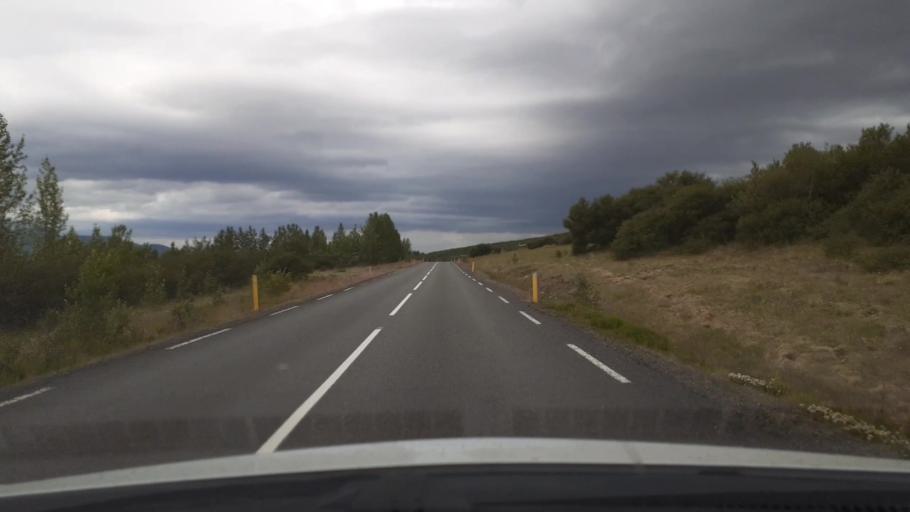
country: IS
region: West
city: Borgarnes
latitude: 64.5417
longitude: -21.5506
